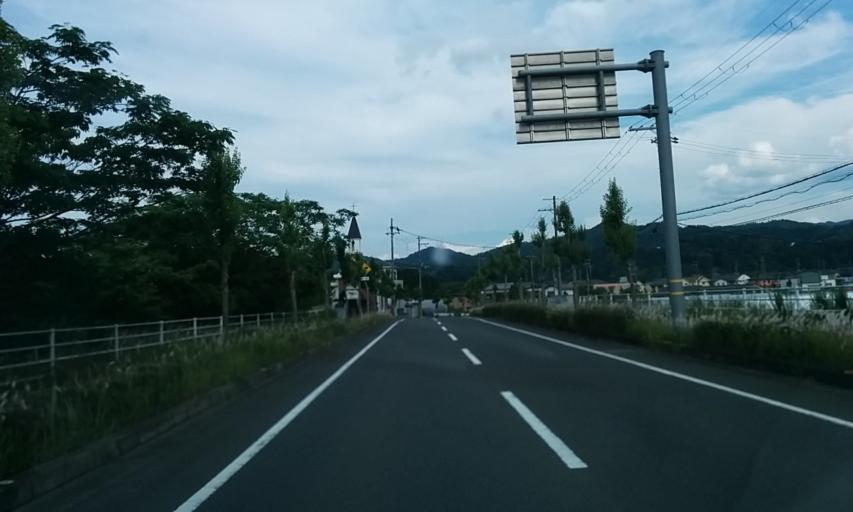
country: JP
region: Kyoto
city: Ayabe
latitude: 35.3078
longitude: 135.2596
